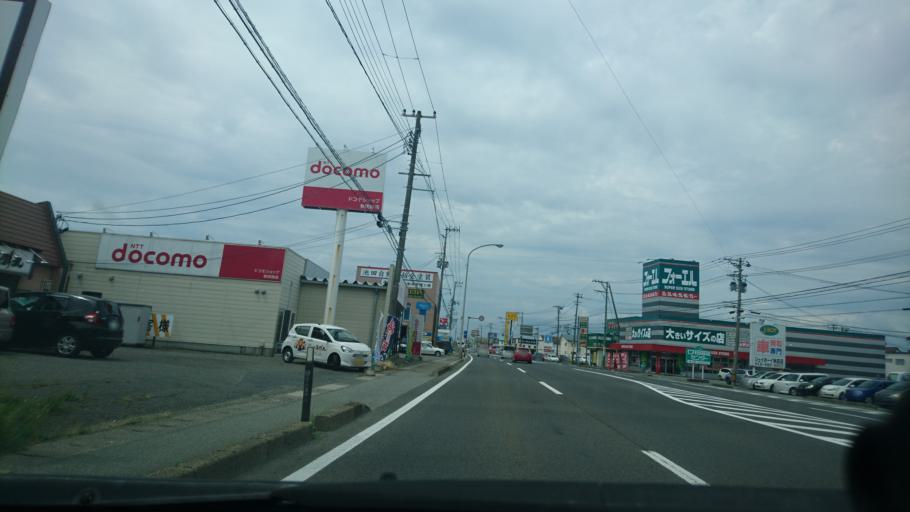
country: JP
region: Akita
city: Akita
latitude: 39.6842
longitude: 140.1254
